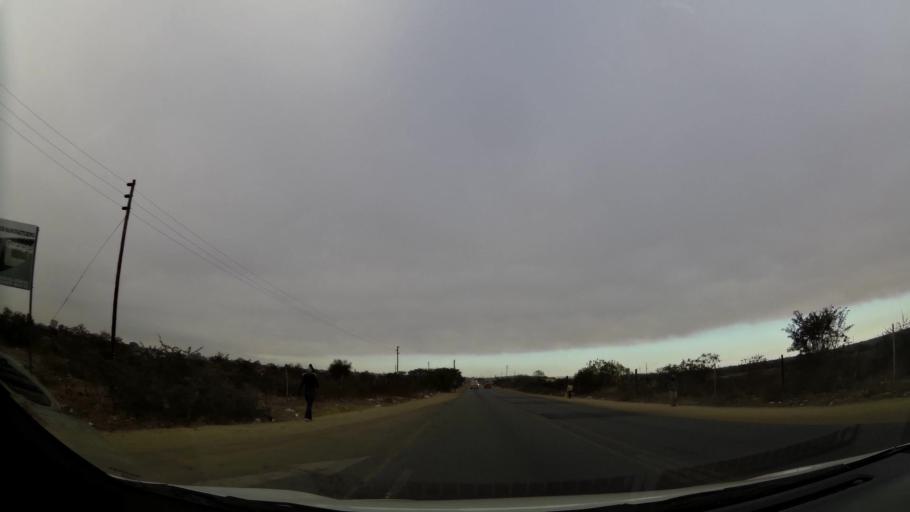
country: ZA
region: Limpopo
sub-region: Capricorn District Municipality
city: Polokwane
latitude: -23.8299
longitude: 29.3797
